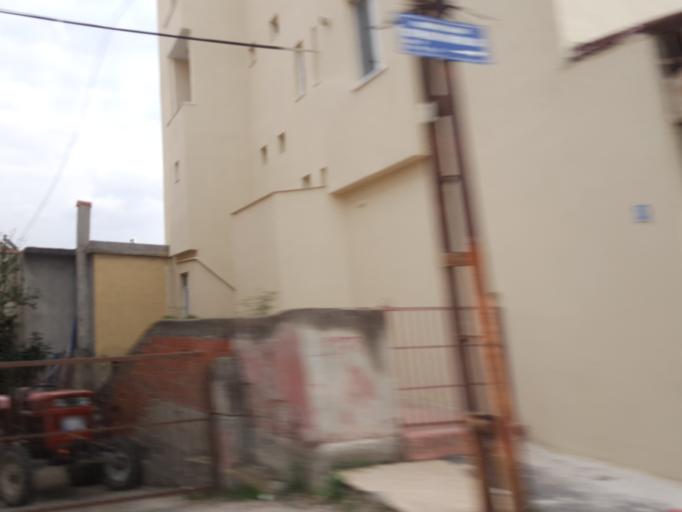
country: TR
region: Sinop
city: Duragan
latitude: 41.4193
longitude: 35.0533
